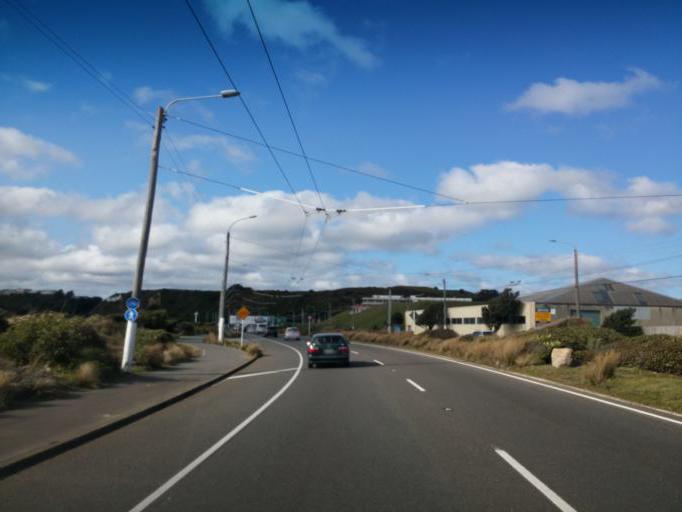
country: NZ
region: Wellington
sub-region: Wellington City
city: Wellington
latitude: -41.3172
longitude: 174.8047
